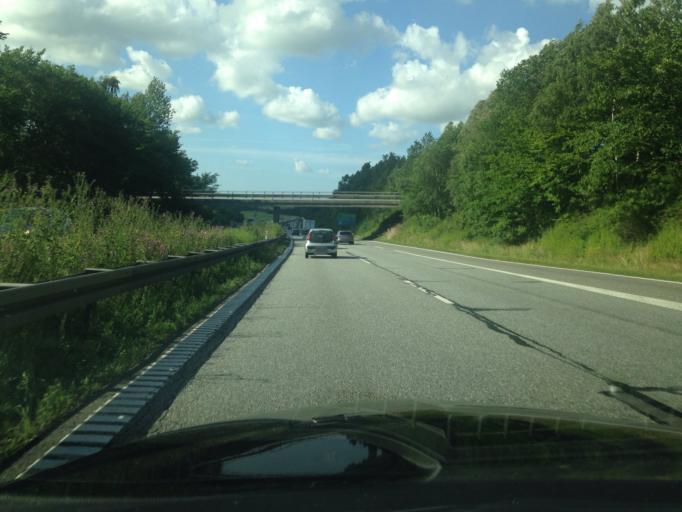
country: DK
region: Capital Region
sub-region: Horsholm Kommune
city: Horsholm
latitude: 55.8772
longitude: 12.4817
